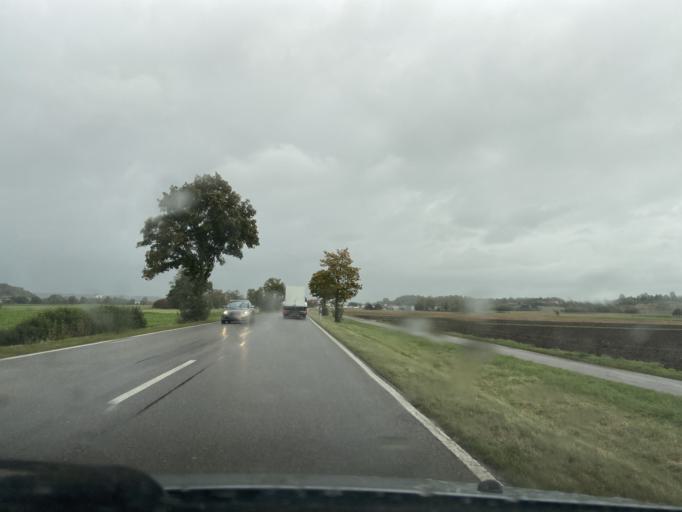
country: DE
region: Baden-Wuerttemberg
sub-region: Tuebingen Region
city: Ennetach
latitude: 48.0367
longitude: 9.3037
